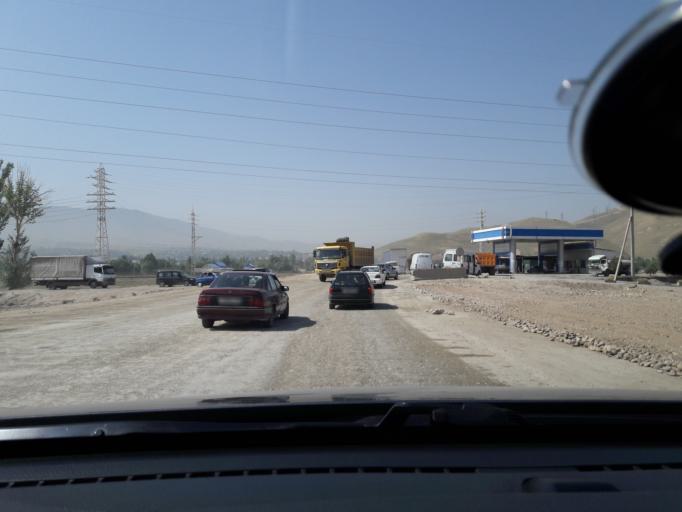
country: TJ
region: Dushanbe
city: Boshkengash
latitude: 38.4537
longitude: 68.7355
